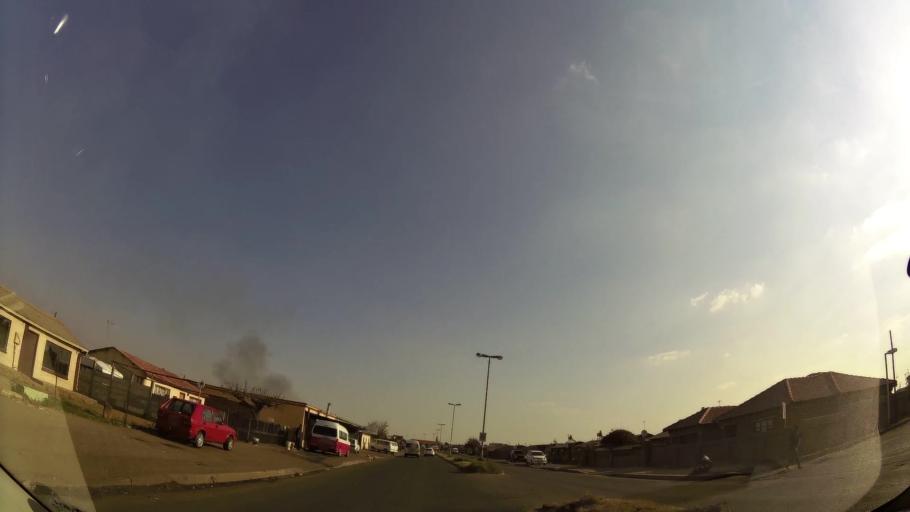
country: ZA
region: Gauteng
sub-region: Ekurhuleni Metropolitan Municipality
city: Brakpan
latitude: -26.1451
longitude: 28.4220
